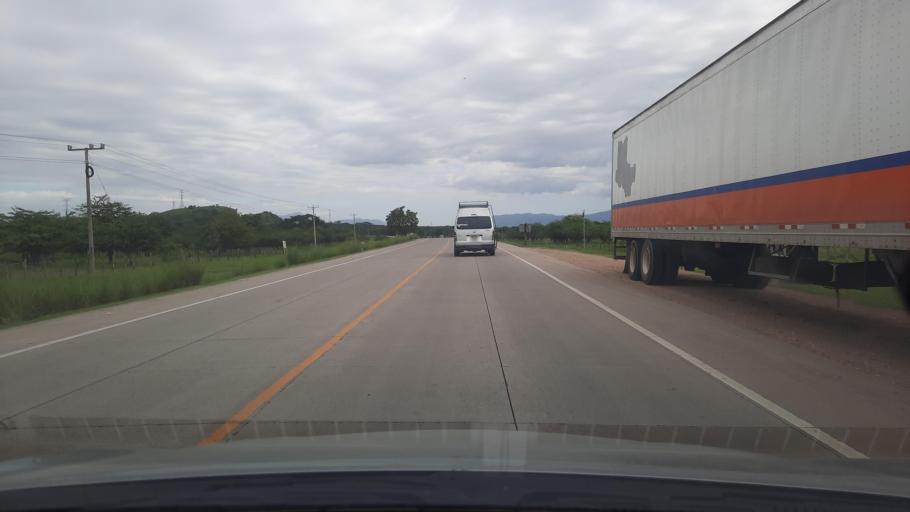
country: NI
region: Chinandega
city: Somotillo
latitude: 12.8795
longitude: -86.8513
